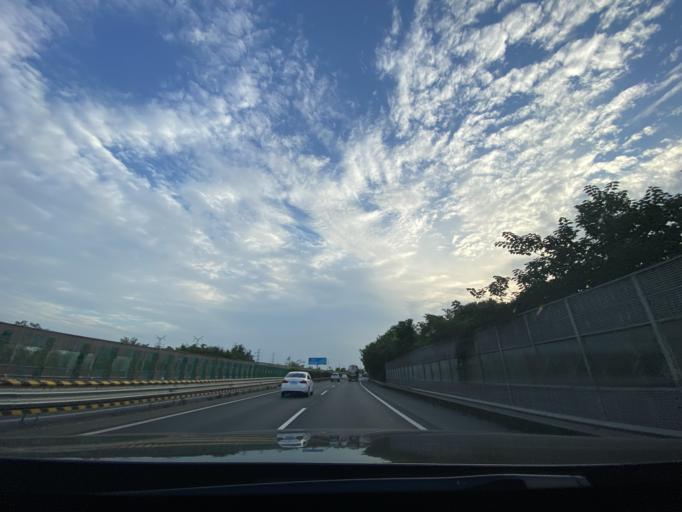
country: CN
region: Sichuan
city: Deyang
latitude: 31.0847
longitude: 104.4056
